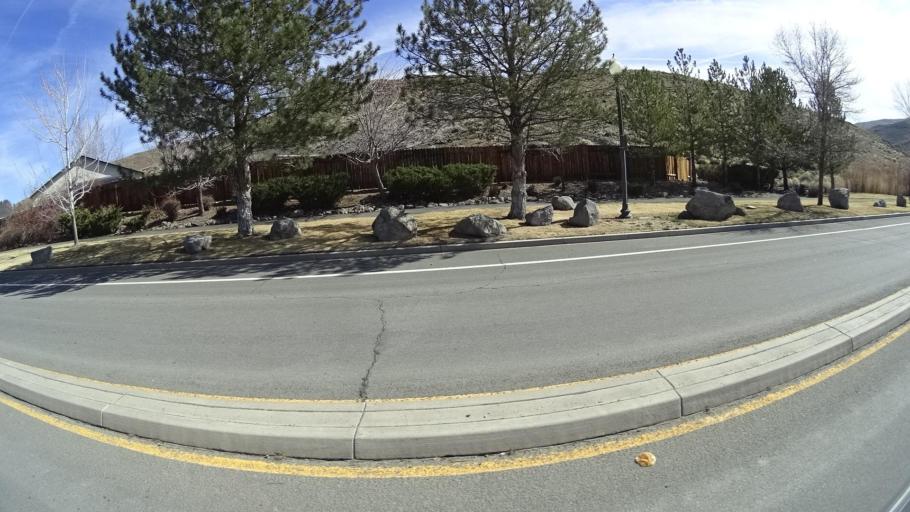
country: US
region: Nevada
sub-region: Washoe County
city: Sparks
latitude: 39.5752
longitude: -119.6966
